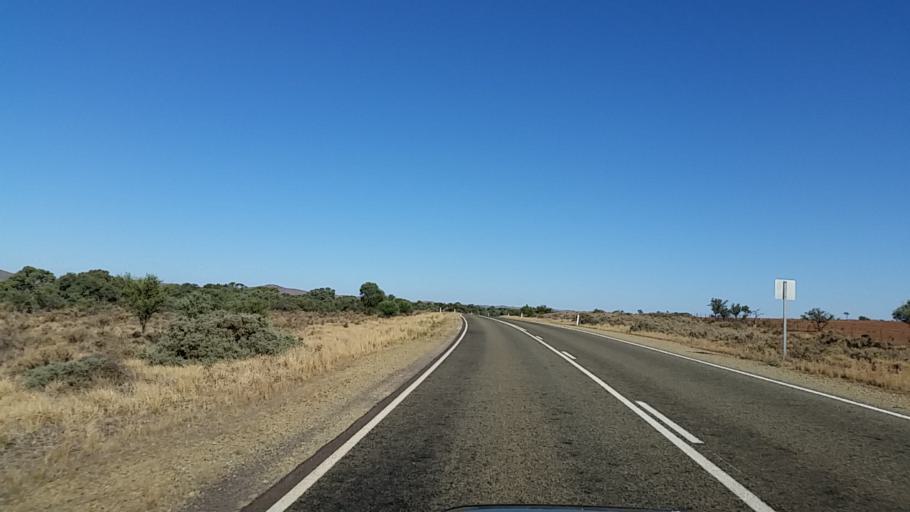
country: AU
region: South Australia
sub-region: Flinders Ranges
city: Quorn
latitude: -32.4130
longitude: 138.5211
